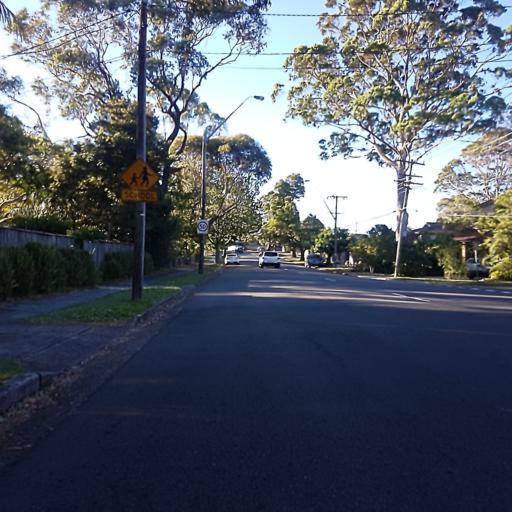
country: AU
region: New South Wales
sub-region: Warringah
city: Davidson
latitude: -33.7432
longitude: 151.2185
